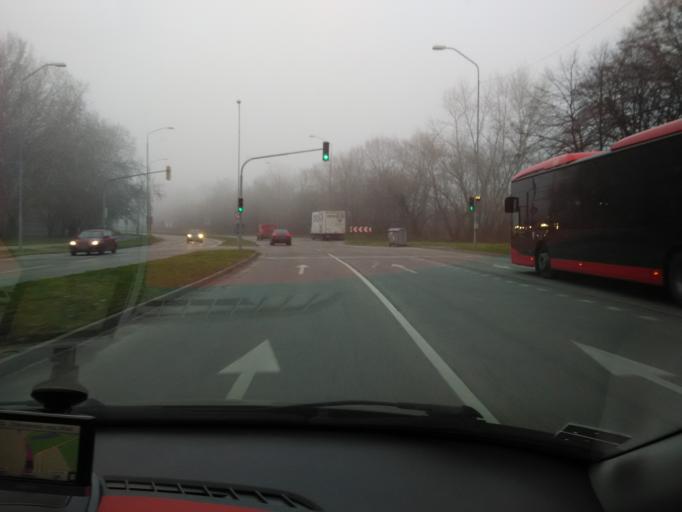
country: SK
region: Bratislavsky
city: Bratislava
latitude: 48.1104
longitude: 17.1139
